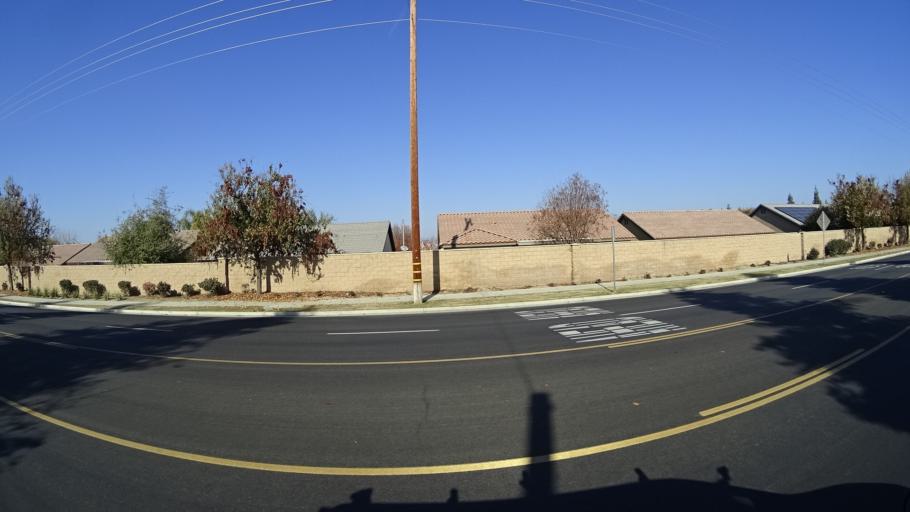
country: US
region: California
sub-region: Kern County
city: Greenacres
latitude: 35.3177
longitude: -119.1169
